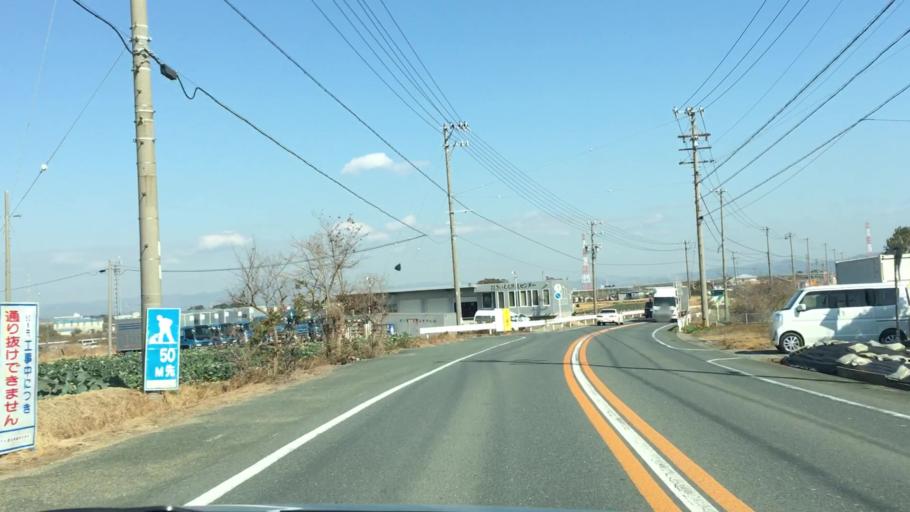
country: JP
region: Aichi
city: Toyohashi
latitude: 34.7009
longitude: 137.3451
